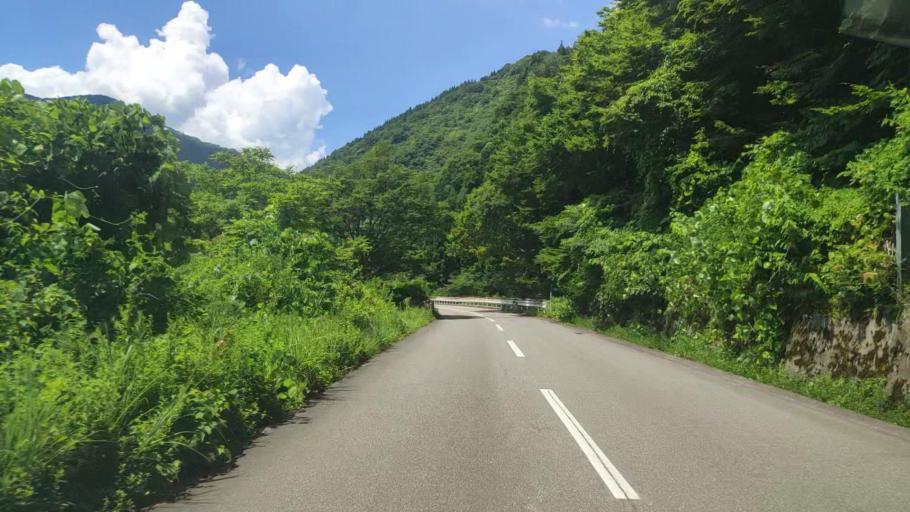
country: JP
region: Fukui
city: Ono
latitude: 35.9029
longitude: 136.5300
